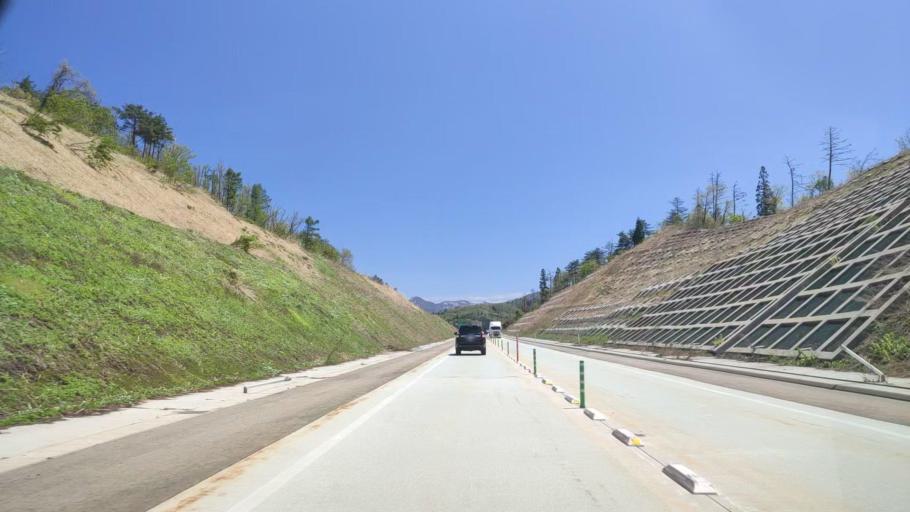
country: JP
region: Yamagata
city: Obanazawa
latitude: 38.5856
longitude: 140.3933
